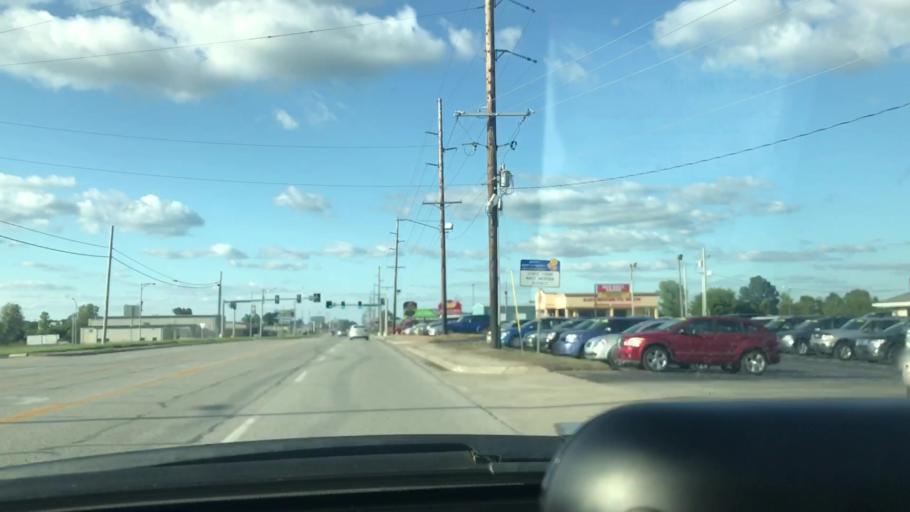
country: US
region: Missouri
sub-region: Pettis County
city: Sedalia
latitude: 38.6729
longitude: -93.2517
